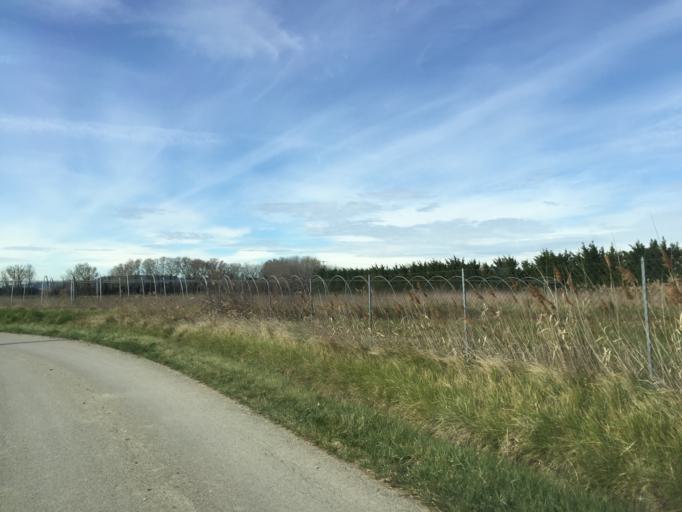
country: FR
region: Provence-Alpes-Cote d'Azur
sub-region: Departement du Vaucluse
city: Caderousse
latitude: 44.1255
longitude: 4.7517
